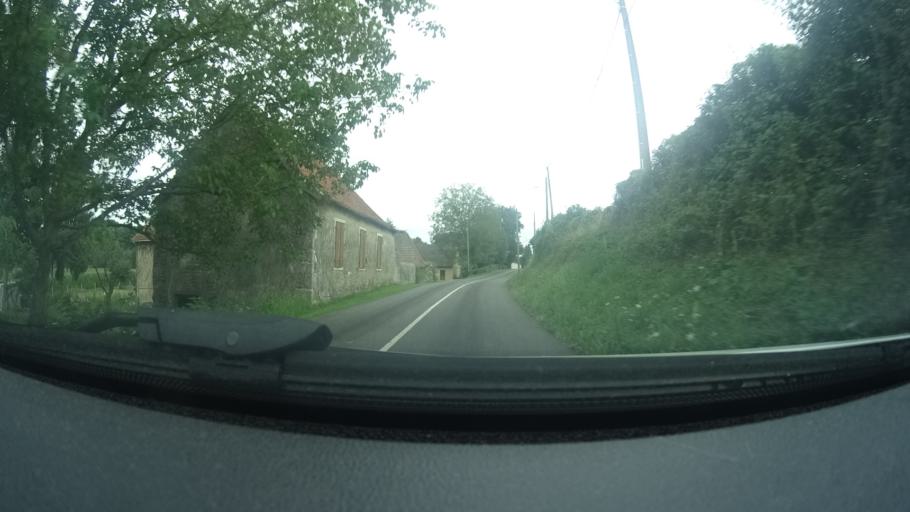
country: FR
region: Aquitaine
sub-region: Departement des Pyrenees-Atlantiques
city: Mont
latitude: 43.4488
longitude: -0.6903
